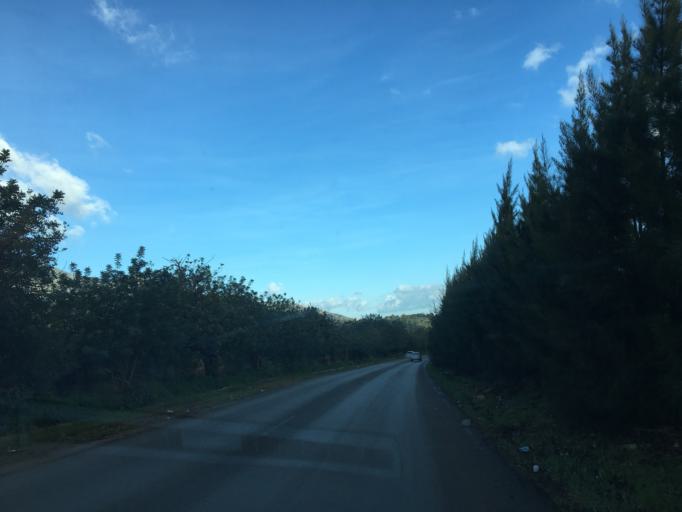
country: DZ
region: Tipaza
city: Tipasa
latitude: 36.5650
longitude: 2.4060
